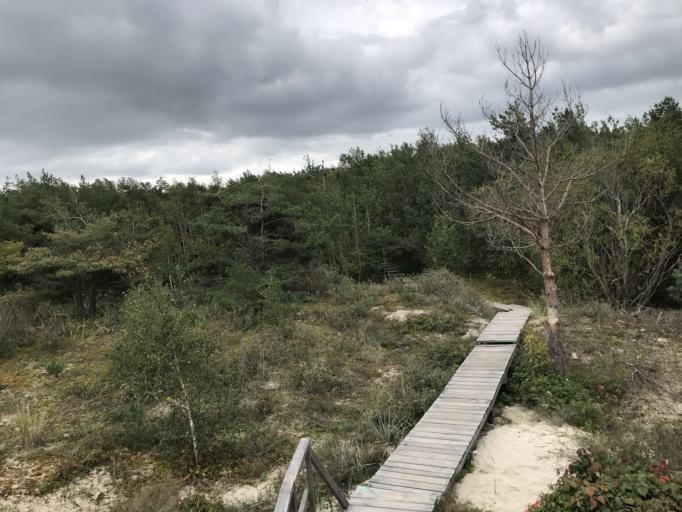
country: LT
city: Nida
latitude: 55.2491
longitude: 20.9219
